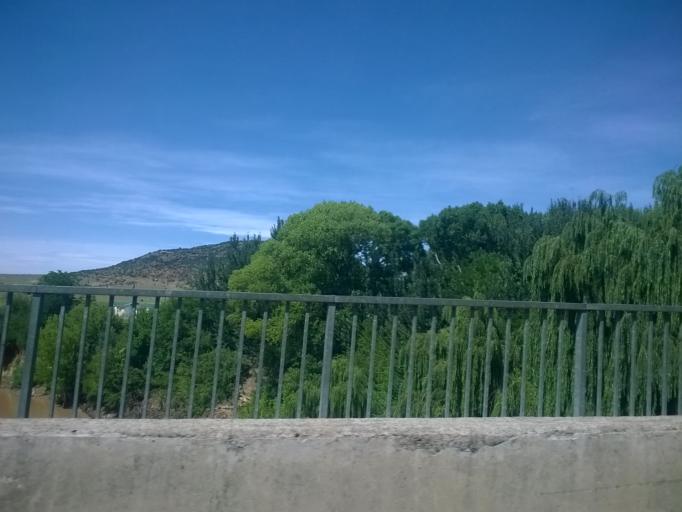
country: LS
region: Maseru
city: Maseru
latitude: -29.2979
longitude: 27.4544
